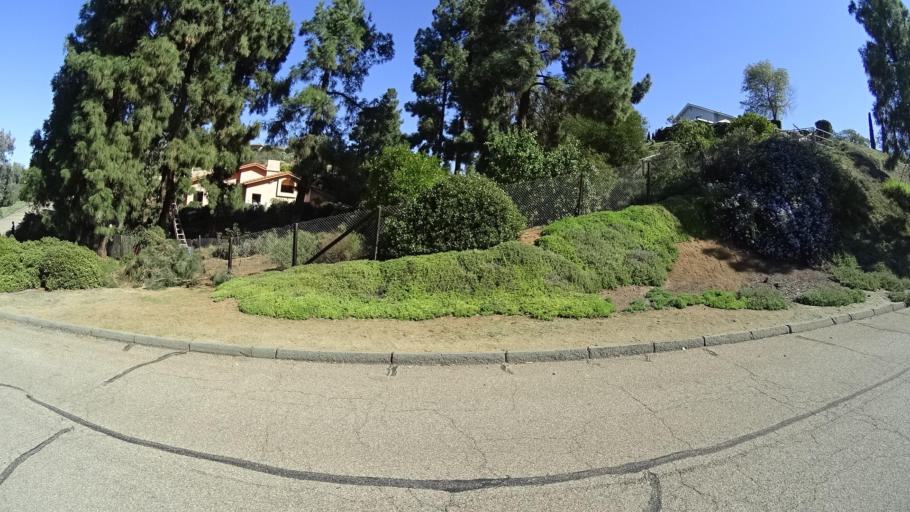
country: US
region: California
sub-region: San Diego County
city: Rancho San Diego
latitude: 32.7302
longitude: -116.9128
